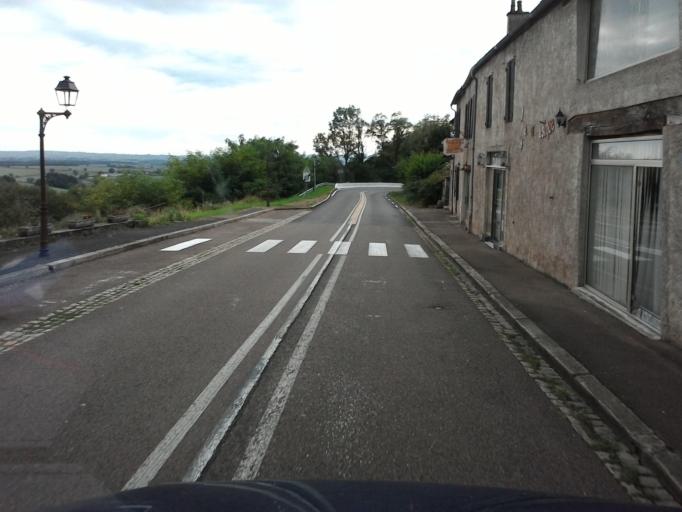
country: FR
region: Bourgogne
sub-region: Departement de Saone-et-Loire
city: Montcenis
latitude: 46.7865
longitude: 4.3876
